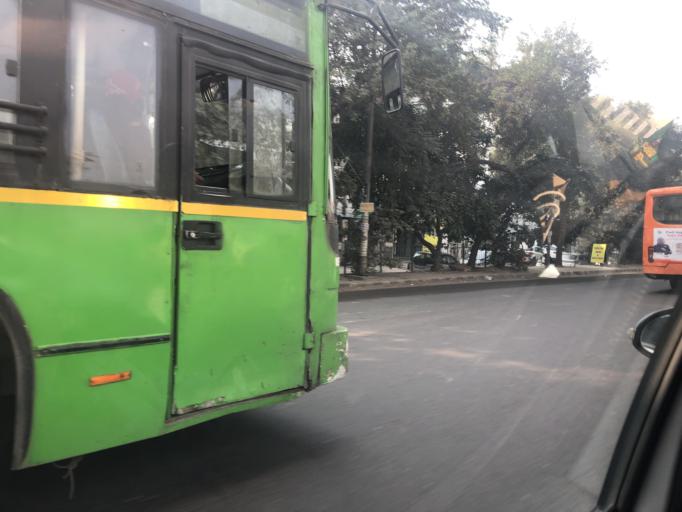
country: IN
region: NCT
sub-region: North West Delhi
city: Pitampura
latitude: 28.6753
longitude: 77.1271
